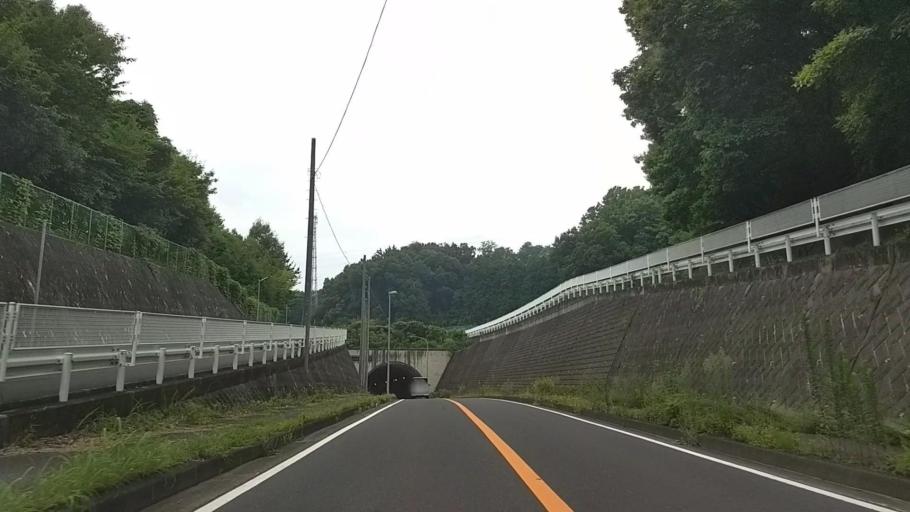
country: JP
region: Kanagawa
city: Hadano
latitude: 35.3391
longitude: 139.2279
